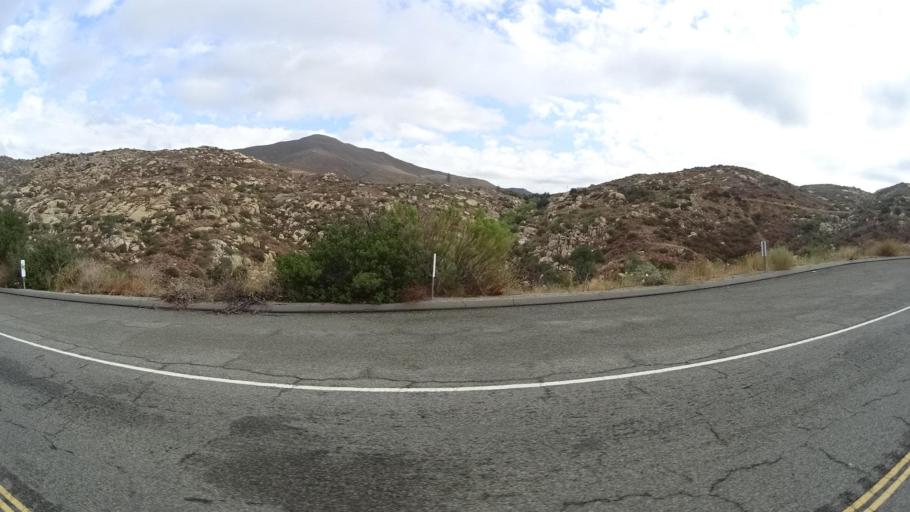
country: MX
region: Baja California
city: Tecate
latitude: 32.6016
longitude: -116.6366
